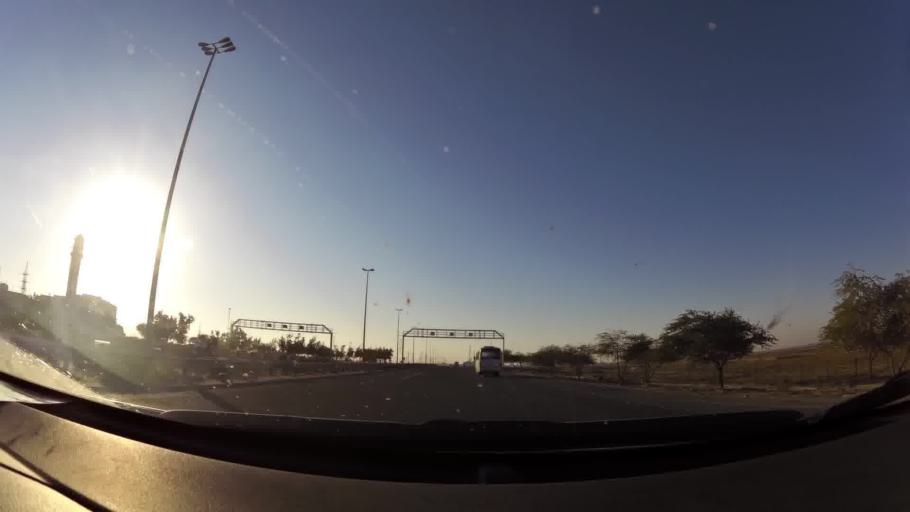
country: KW
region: Al Ahmadi
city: Al Wafrah
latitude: 28.7450
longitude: 48.2830
